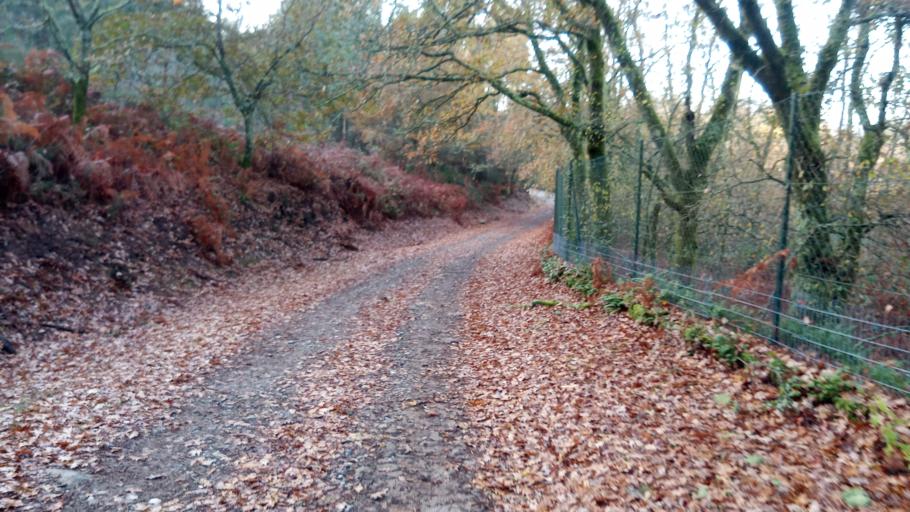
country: PT
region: Viana do Castelo
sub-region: Paredes de Coura
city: Paredes de Coura
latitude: 41.8941
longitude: -8.6139
